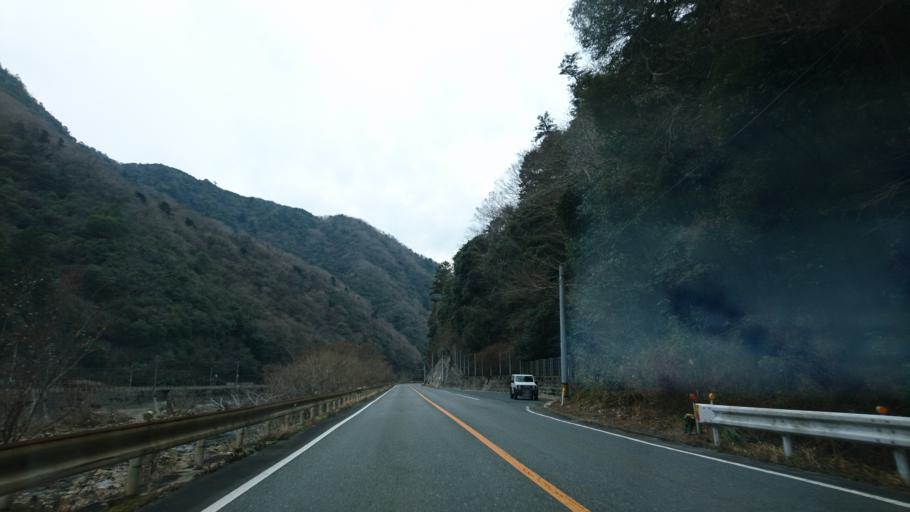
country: JP
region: Okayama
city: Niimi
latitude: 34.8979
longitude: 133.5409
